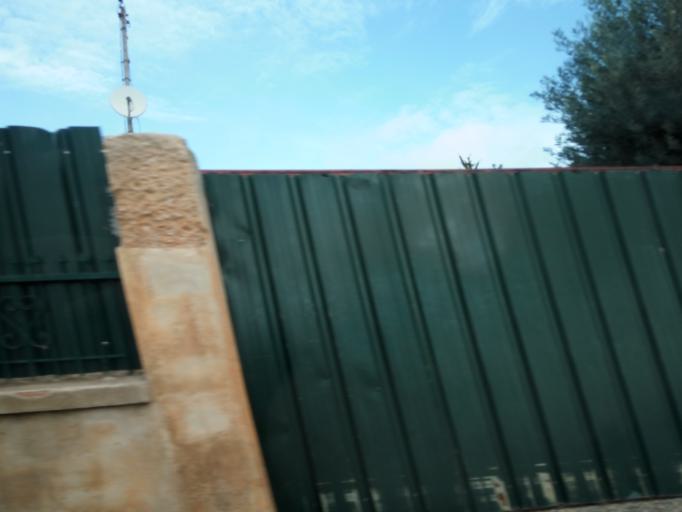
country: PT
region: Faro
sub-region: Faro
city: Santa Barbara de Nexe
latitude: 37.0886
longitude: -7.9594
